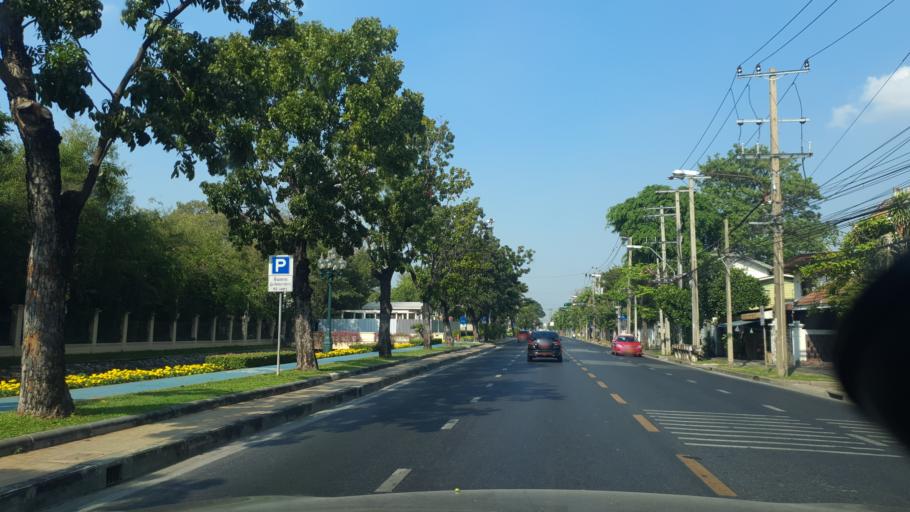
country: TH
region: Bangkok
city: Dusit
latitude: 13.7723
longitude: 100.5219
